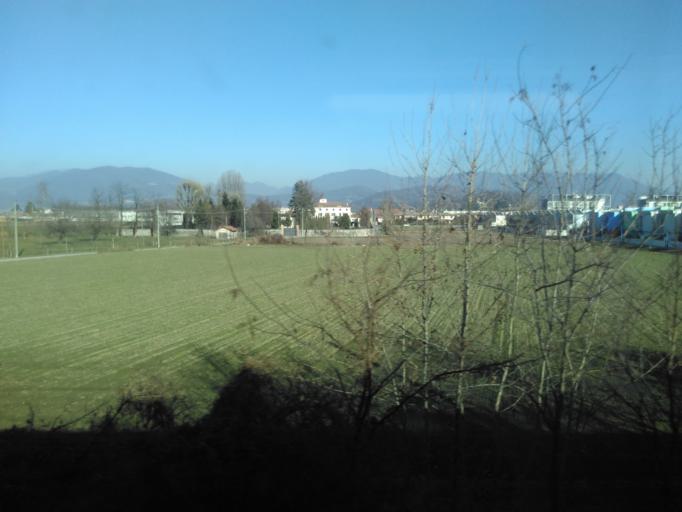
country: IT
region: Lombardy
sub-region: Provincia di Brescia
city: Roncadelle
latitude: 45.5413
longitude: 10.1608
